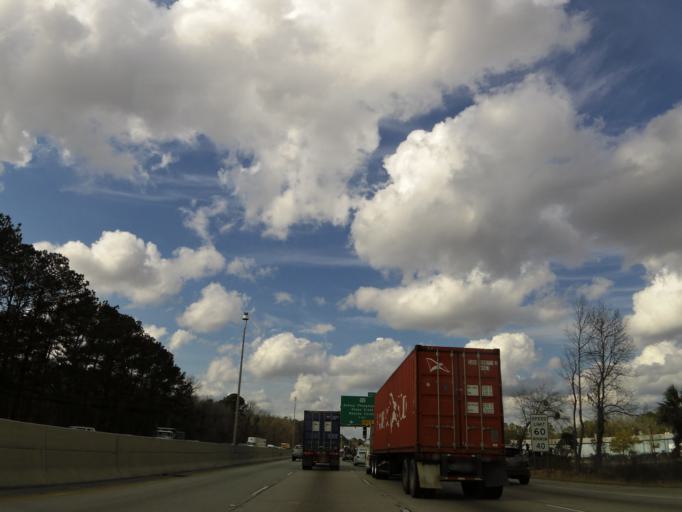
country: US
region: South Carolina
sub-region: Berkeley County
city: Hanahan
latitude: 32.9172
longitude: -80.0330
